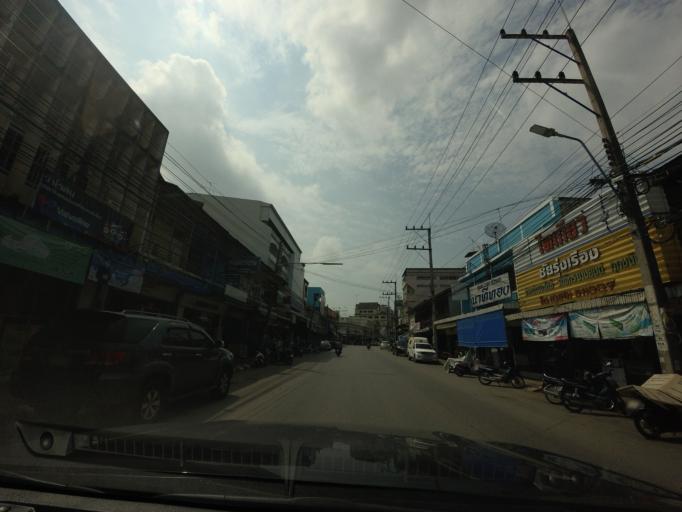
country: TH
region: Phrae
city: Phrae
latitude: 18.1400
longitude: 100.1482
